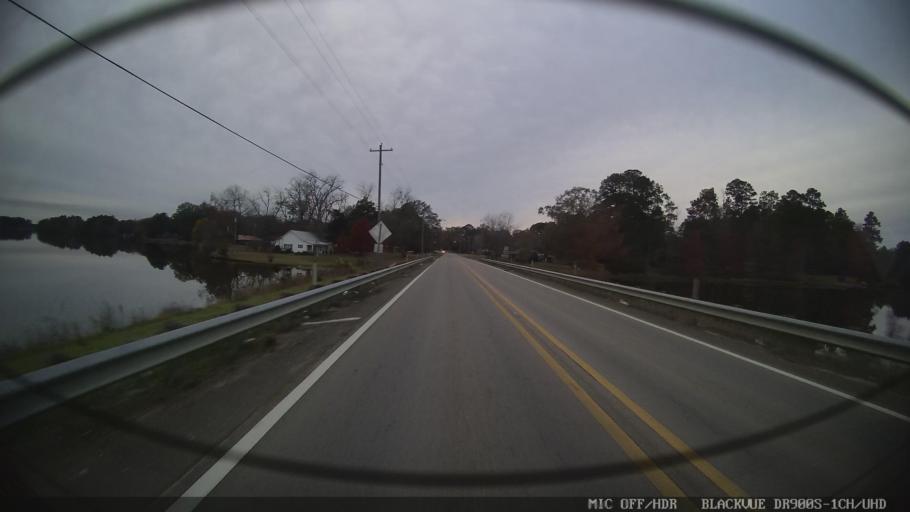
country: US
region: Mississippi
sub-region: Clarke County
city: Quitman
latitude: 32.0394
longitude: -88.7117
